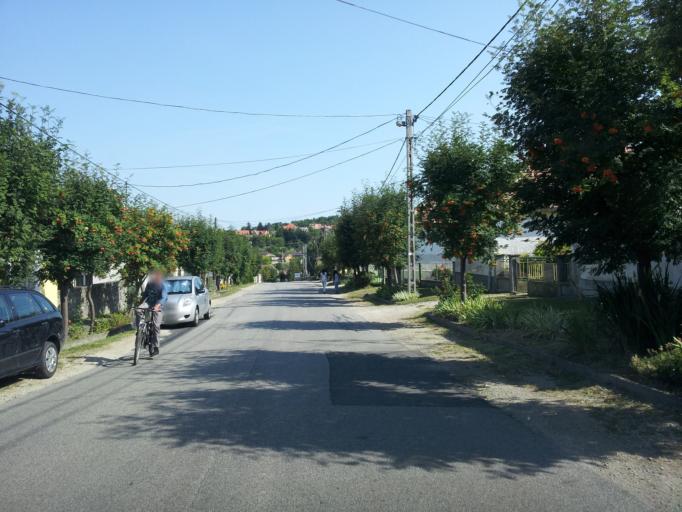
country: HU
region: Zala
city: Cserszegtomaj
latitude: 46.8416
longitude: 17.2190
